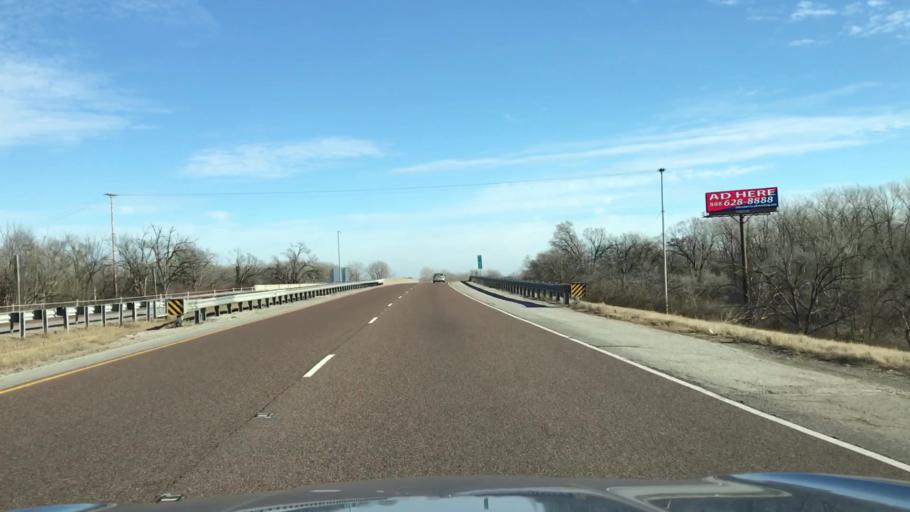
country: US
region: Illinois
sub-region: Madison County
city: Mitchell
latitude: 38.7660
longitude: -90.1176
